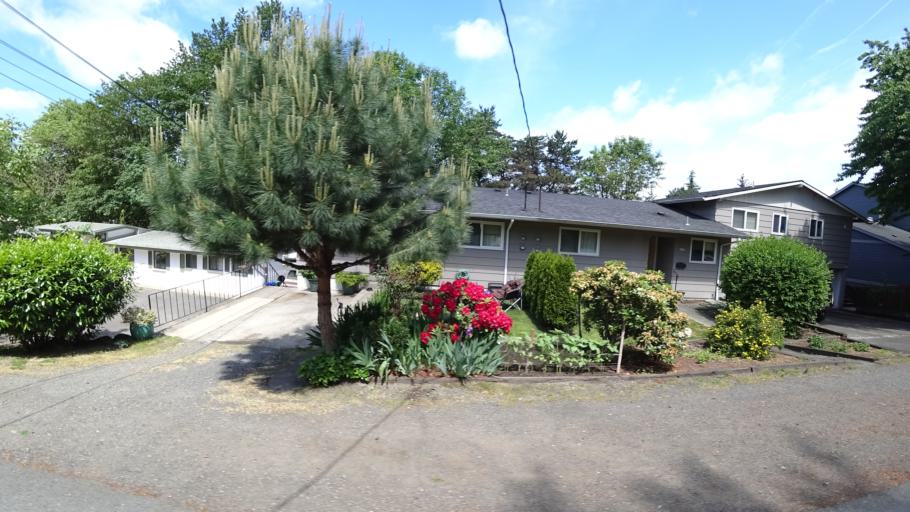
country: US
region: Oregon
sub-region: Washington County
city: Garden Home-Whitford
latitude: 45.4666
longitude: -122.7187
